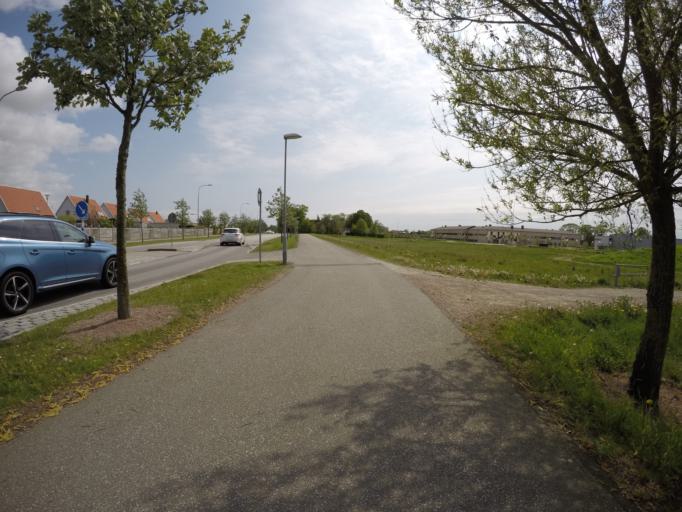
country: SE
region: Skane
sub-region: Malmo
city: Tygelsjo
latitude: 55.5216
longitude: 12.9972
